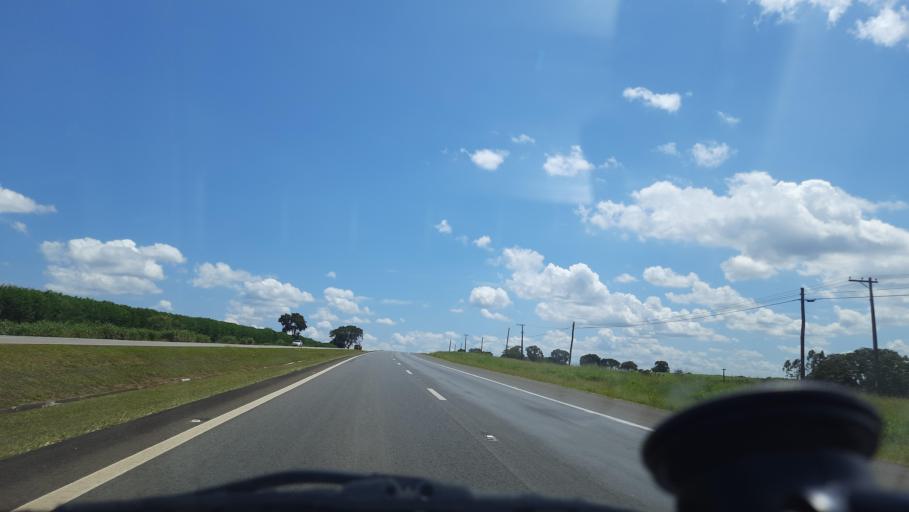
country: BR
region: Sao Paulo
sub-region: Moji-Guacu
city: Mogi-Gaucu
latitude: -22.2590
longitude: -46.9764
